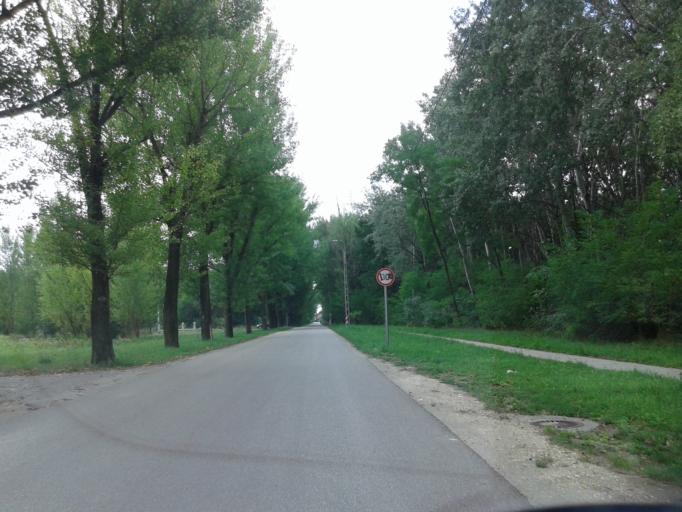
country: HU
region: Csongrad
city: Domaszek
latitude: 46.2743
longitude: 20.0306
